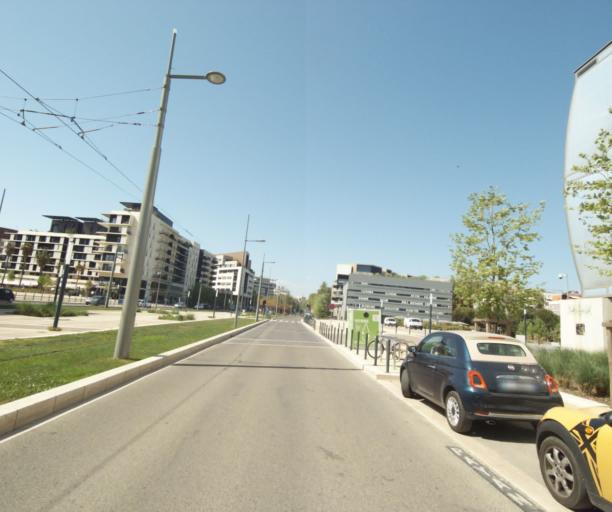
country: FR
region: Languedoc-Roussillon
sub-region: Departement de l'Herault
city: Montpellier
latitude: 43.5996
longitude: 3.9025
